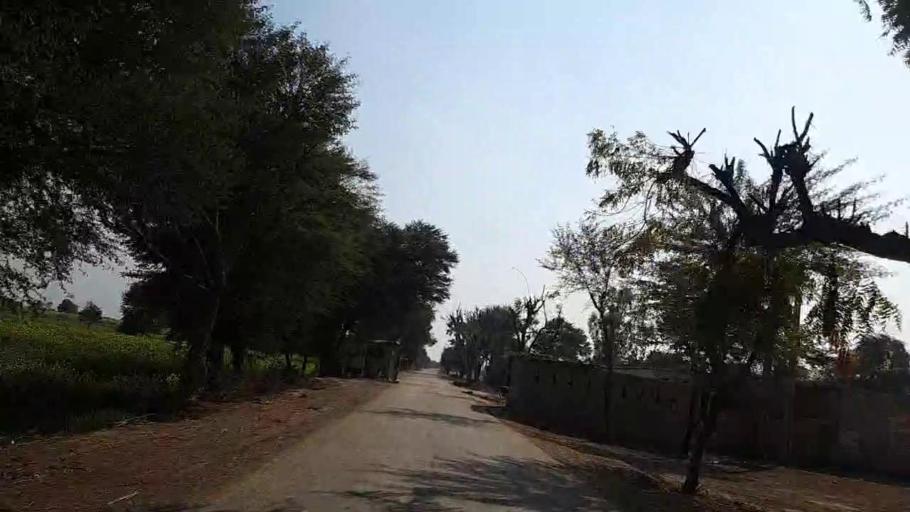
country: PK
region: Sindh
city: Sakrand
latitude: 26.0629
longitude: 68.2895
